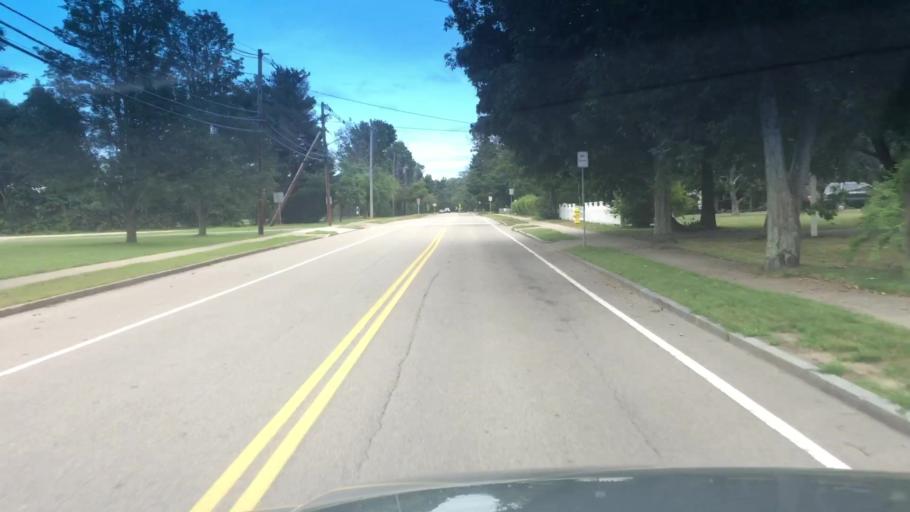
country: US
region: Massachusetts
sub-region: Norfolk County
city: Westwood
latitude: 42.2069
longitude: -71.2366
